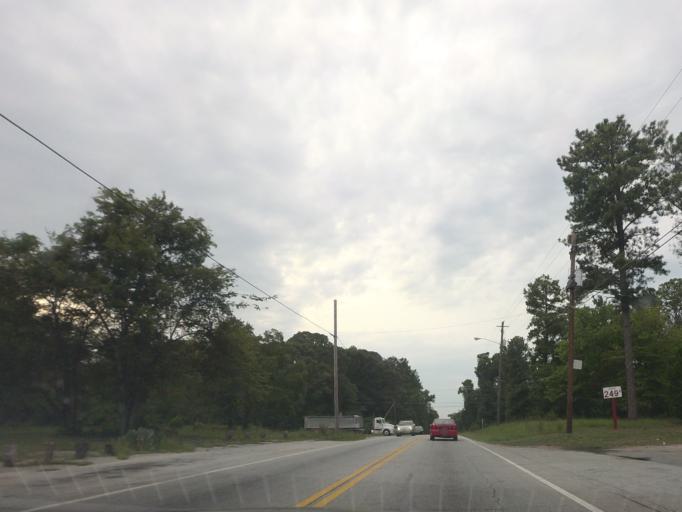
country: US
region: Georgia
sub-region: Bibb County
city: Macon
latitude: 32.8139
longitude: -83.5183
